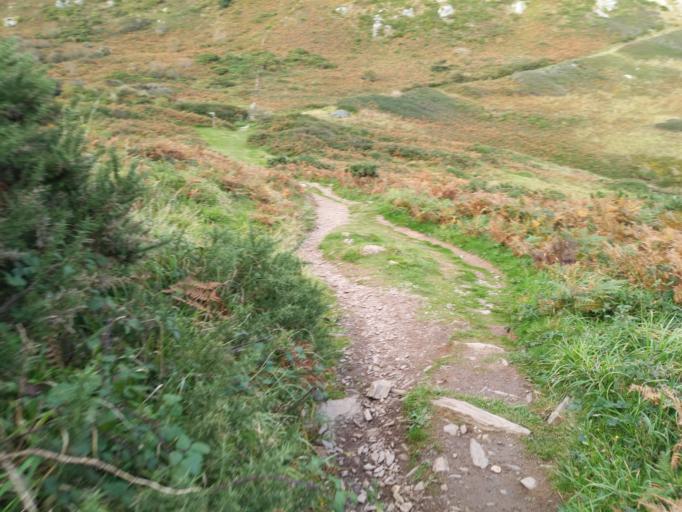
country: GB
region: England
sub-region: Devon
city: Salcombe
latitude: 50.2148
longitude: -3.7880
